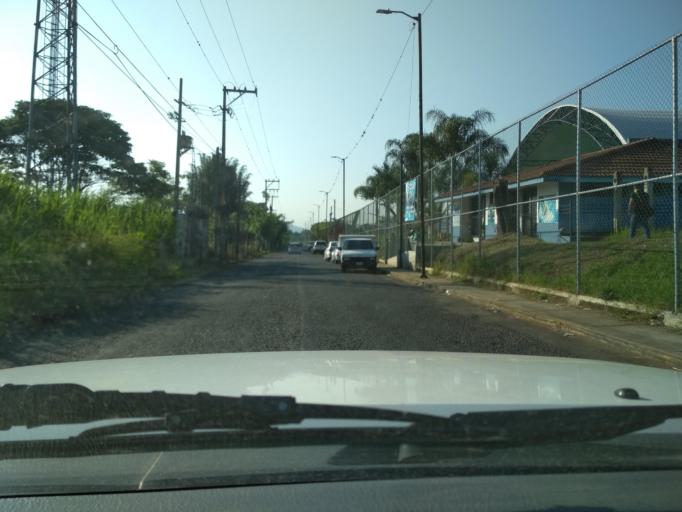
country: MX
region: Veracruz
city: Cordoba
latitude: 18.8692
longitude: -96.9271
